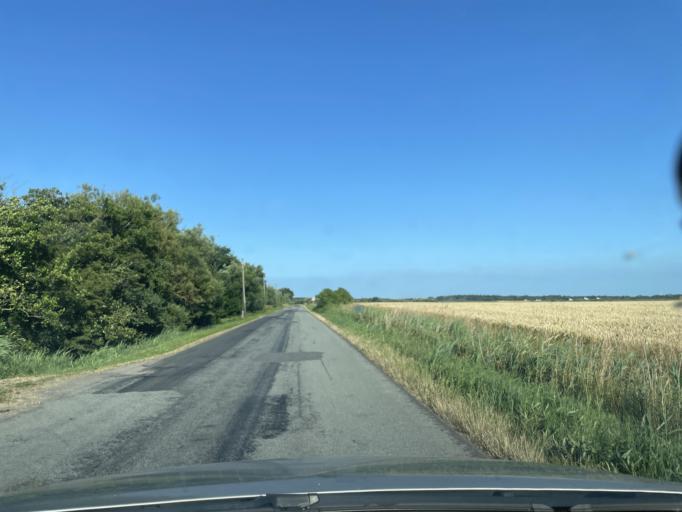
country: DE
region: Schleswig-Holstein
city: Aventoft
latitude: 54.8773
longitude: 8.8305
